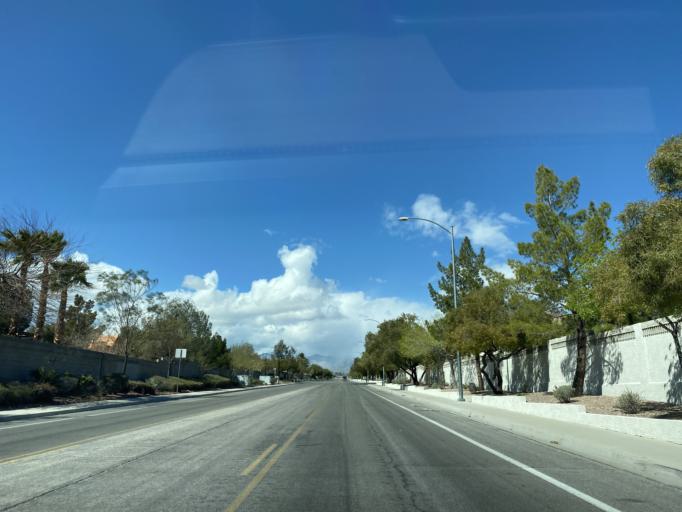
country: US
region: Nevada
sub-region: Clark County
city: Summerlin South
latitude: 36.3214
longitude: -115.2902
